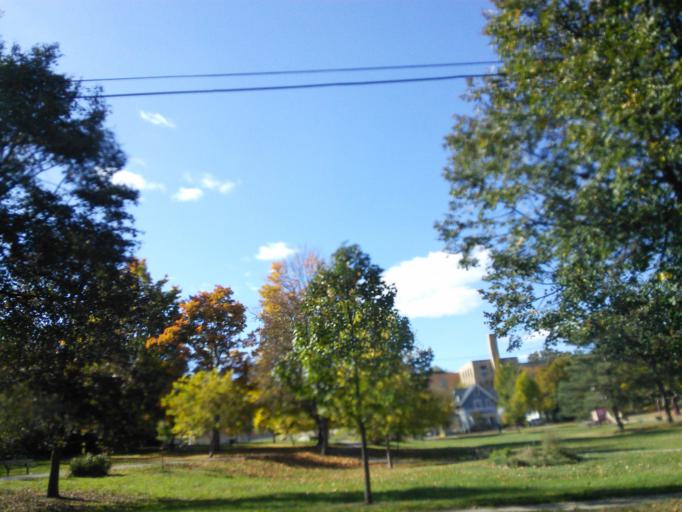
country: US
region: Michigan
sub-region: Washtenaw County
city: Ann Arbor
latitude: 42.2795
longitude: -83.7586
